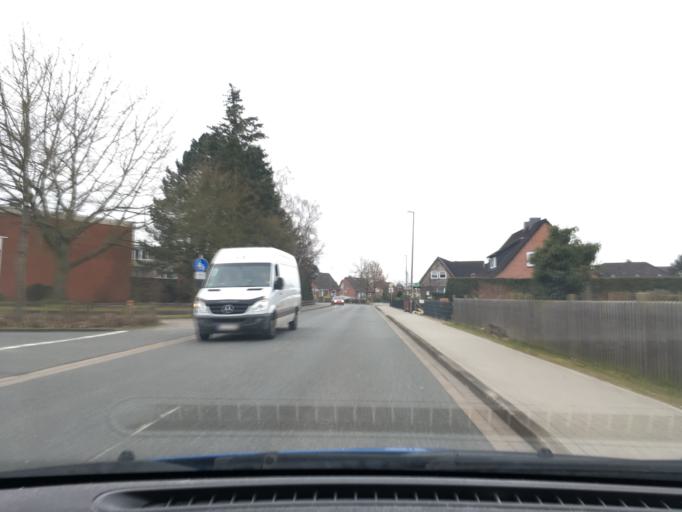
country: DE
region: Lower Saxony
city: Vogelsen
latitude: 53.2757
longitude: 10.3523
